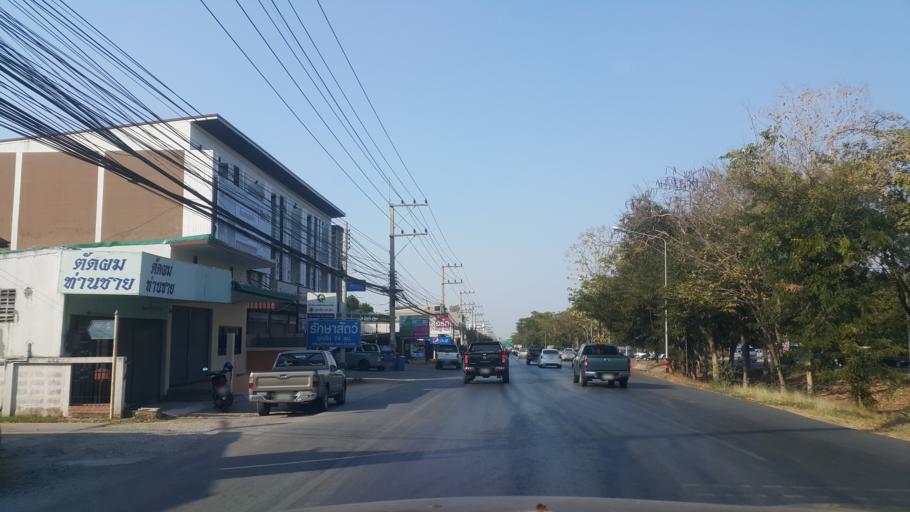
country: TH
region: Nakhon Ratchasima
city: Nakhon Ratchasima
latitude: 14.9405
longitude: 102.0538
